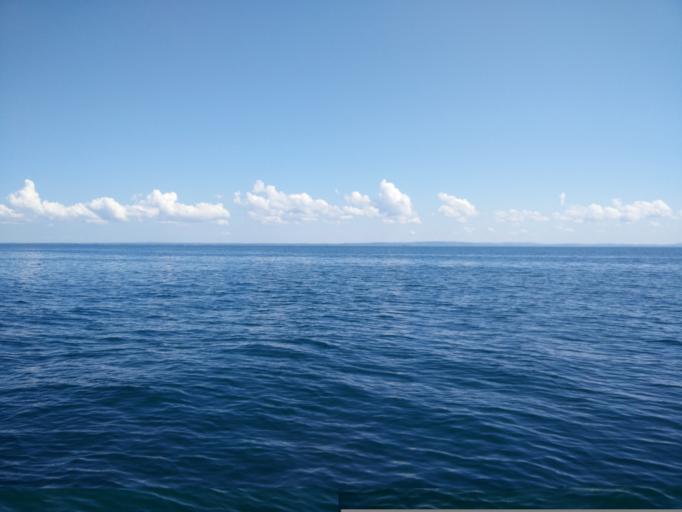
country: MM
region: Ayeyarwady
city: Pathein
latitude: 16.8752
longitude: 94.2669
